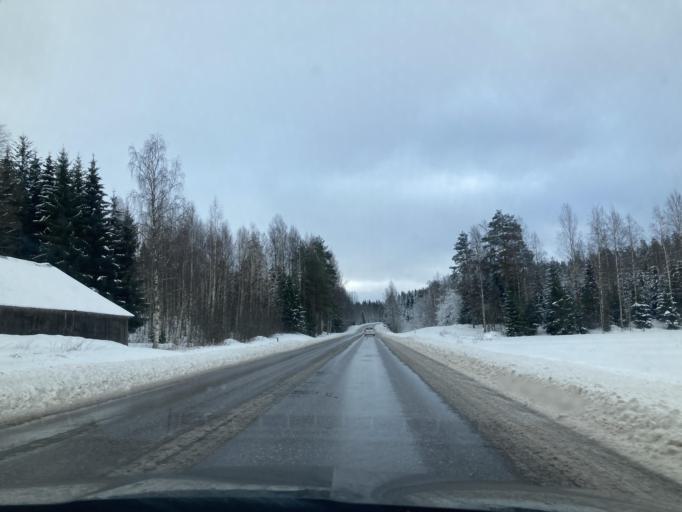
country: FI
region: Paijanne Tavastia
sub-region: Lahti
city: Padasjoki
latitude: 61.3376
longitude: 25.2618
